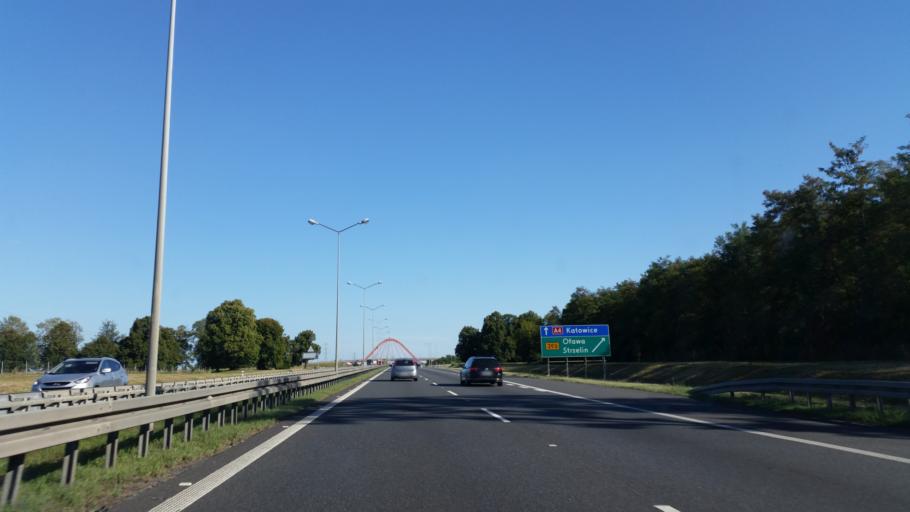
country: PL
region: Lower Silesian Voivodeship
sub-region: Powiat olawski
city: Wierzbno
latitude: 50.8822
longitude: 17.1980
